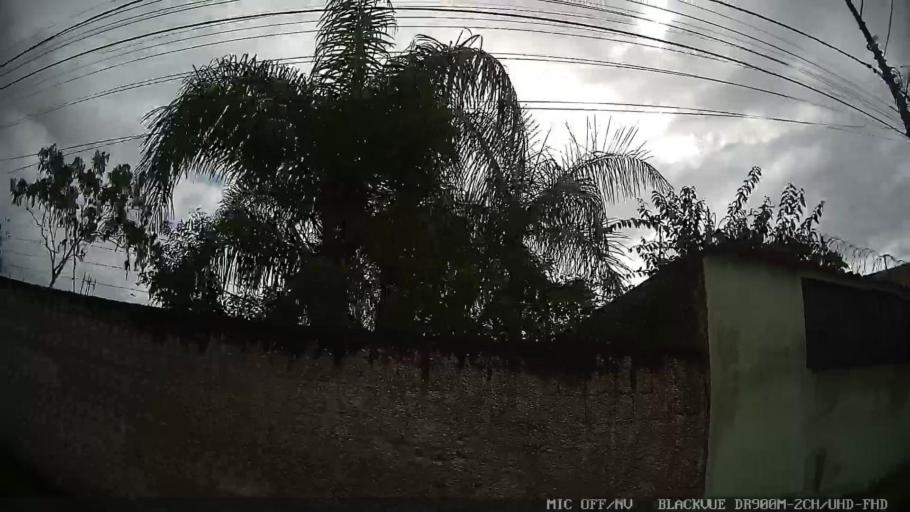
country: BR
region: Sao Paulo
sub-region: Itanhaem
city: Itanhaem
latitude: -24.1877
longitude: -46.8165
